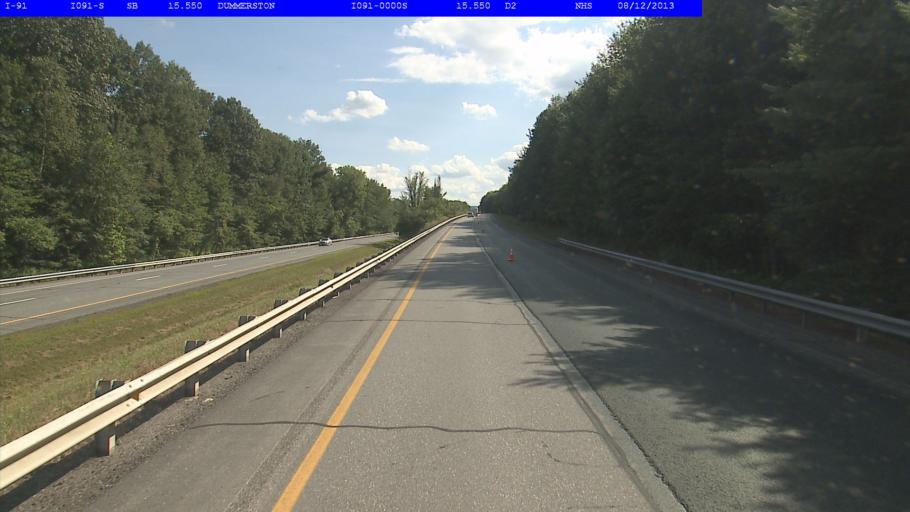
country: US
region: New Hampshire
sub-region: Cheshire County
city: Chesterfield
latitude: 42.9342
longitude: -72.5279
